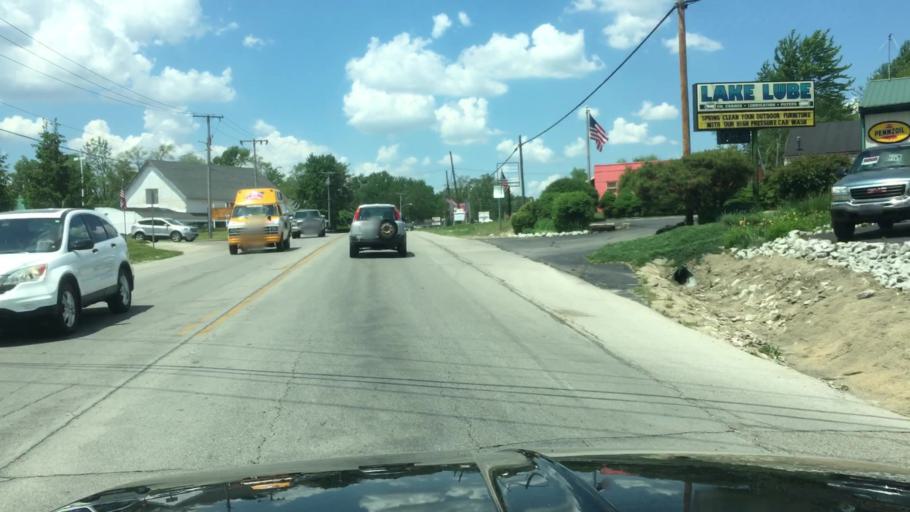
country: US
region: Indiana
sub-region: Kosciusko County
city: North Webster
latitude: 41.3208
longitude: -85.6964
